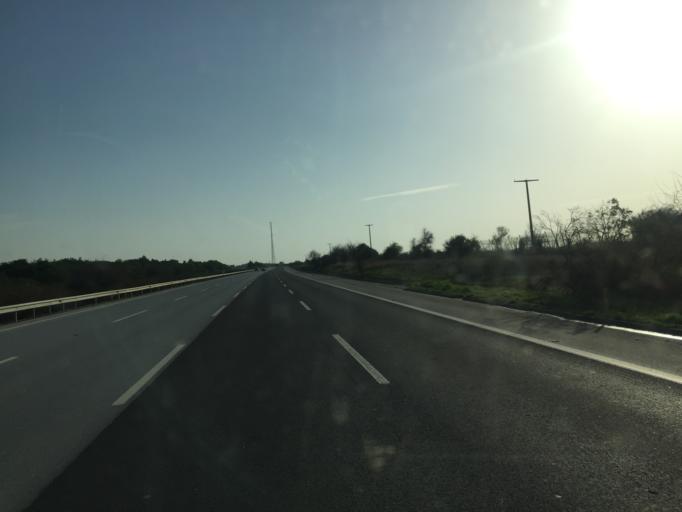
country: TR
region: Mersin
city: Yenice
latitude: 37.0232
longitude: 35.0736
